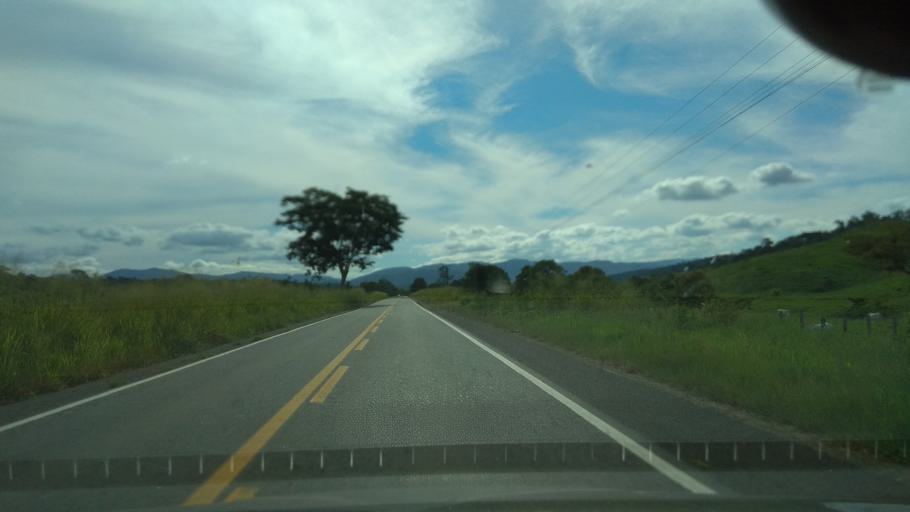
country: BR
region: Bahia
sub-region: Jitauna
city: Jitauna
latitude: -14.0398
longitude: -39.8252
